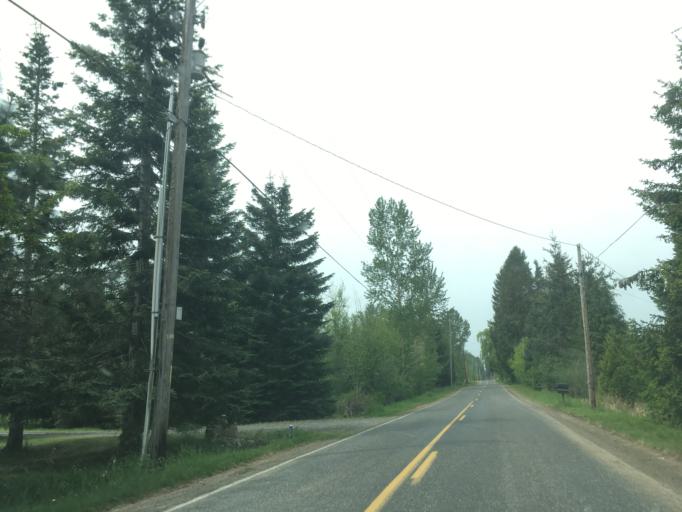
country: US
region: Washington
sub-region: Whatcom County
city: Geneva
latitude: 48.8188
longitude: -122.4091
